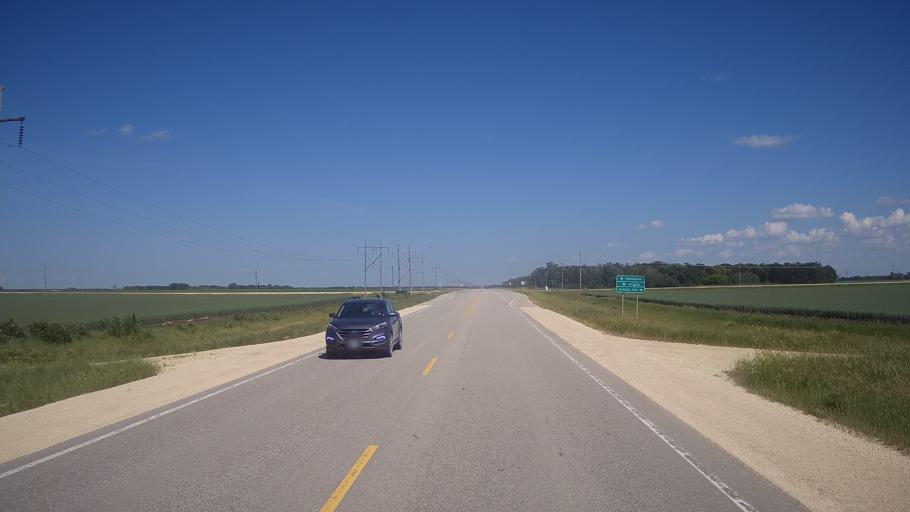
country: CA
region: Manitoba
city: Stonewall
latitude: 50.1227
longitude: -97.4409
